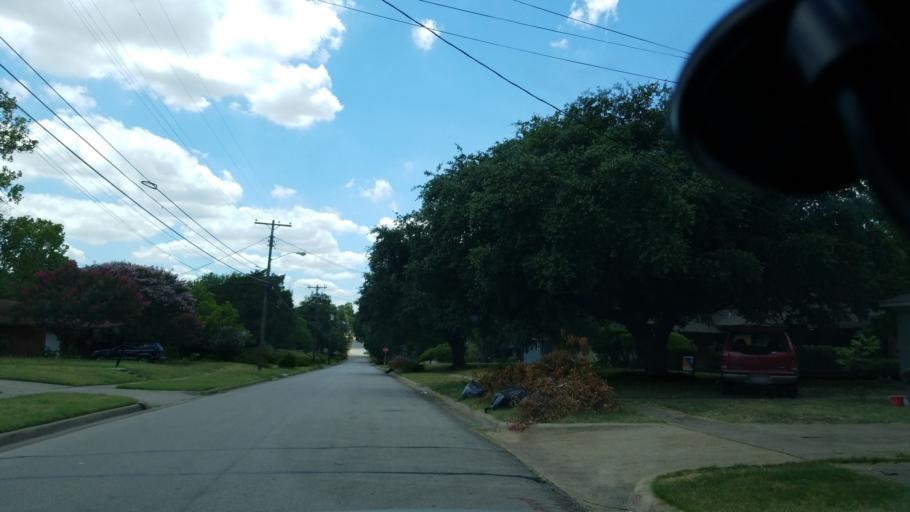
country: US
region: Texas
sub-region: Dallas County
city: Cockrell Hill
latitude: 32.7000
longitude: -96.8585
